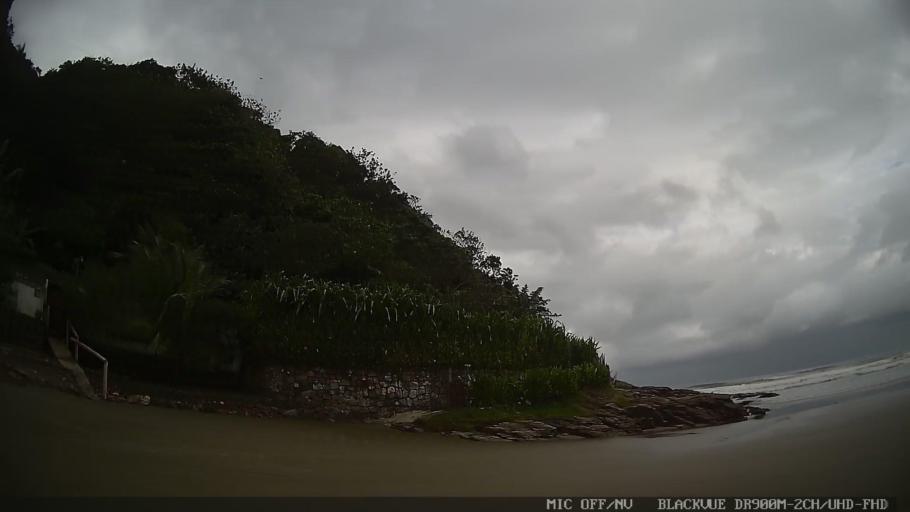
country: BR
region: Sao Paulo
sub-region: Itanhaem
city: Itanhaem
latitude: -24.1906
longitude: -46.7929
